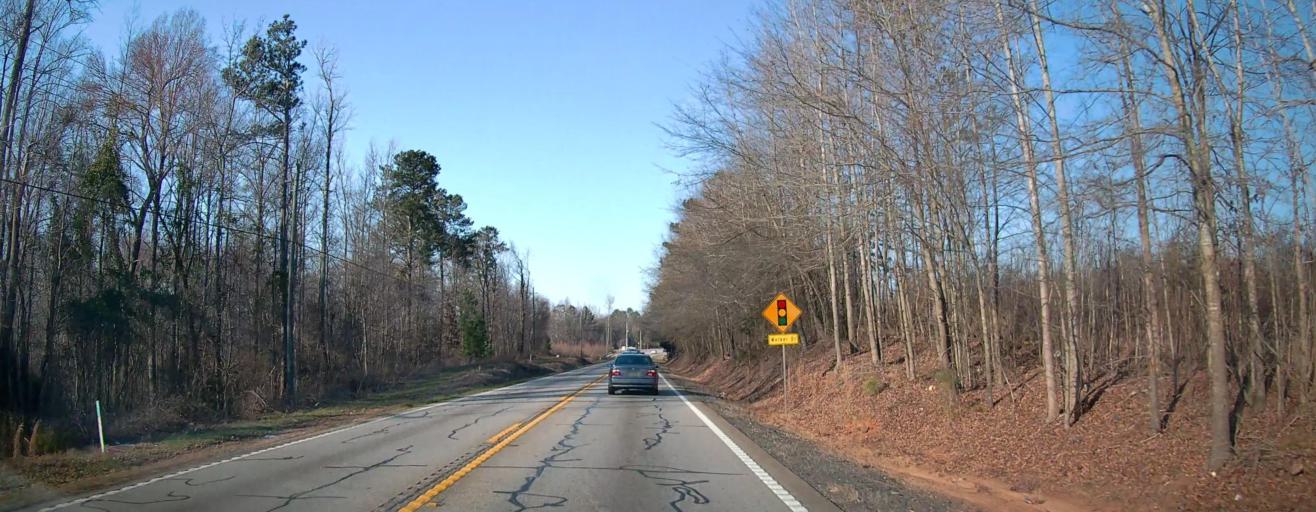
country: US
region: Georgia
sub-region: Henry County
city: McDonough
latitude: 33.3781
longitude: -84.1786
